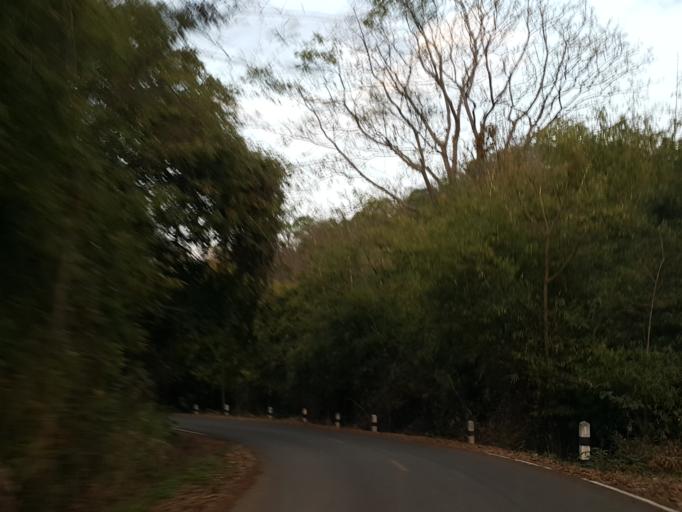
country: TH
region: Lampang
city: Mueang Pan
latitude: 18.8234
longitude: 99.4544
